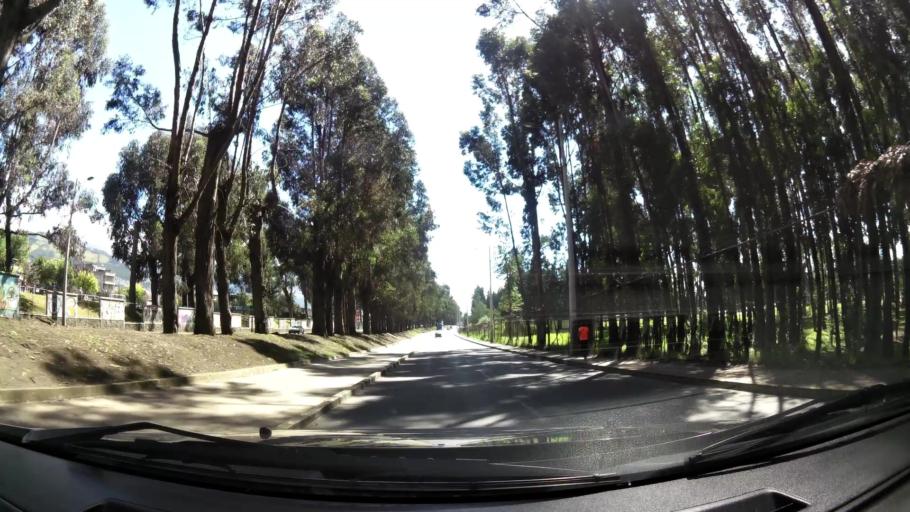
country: EC
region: Pichincha
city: Quito
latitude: -0.2873
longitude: -78.5564
